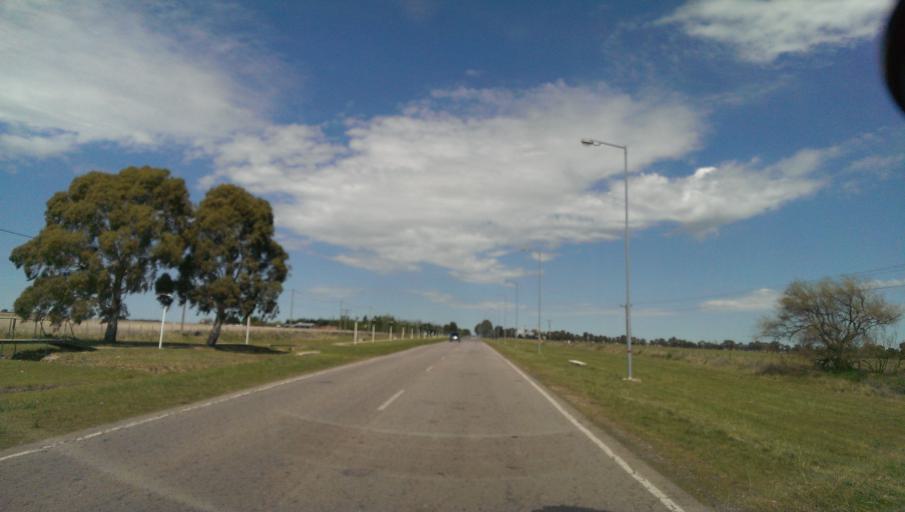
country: AR
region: Buenos Aires
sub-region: Partido de Tornquist
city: Tornquist
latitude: -38.0794
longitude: -62.2202
